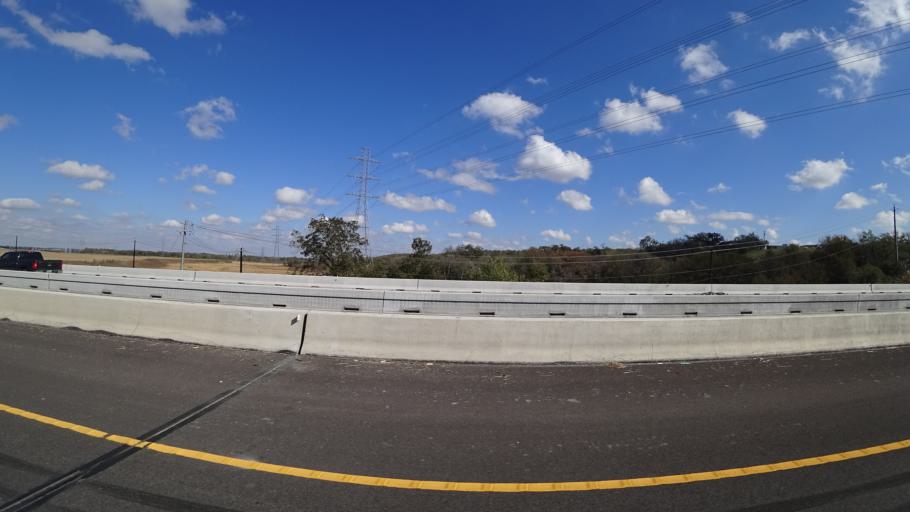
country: US
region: Texas
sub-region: Travis County
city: Garfield
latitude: 30.1894
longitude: -97.6186
